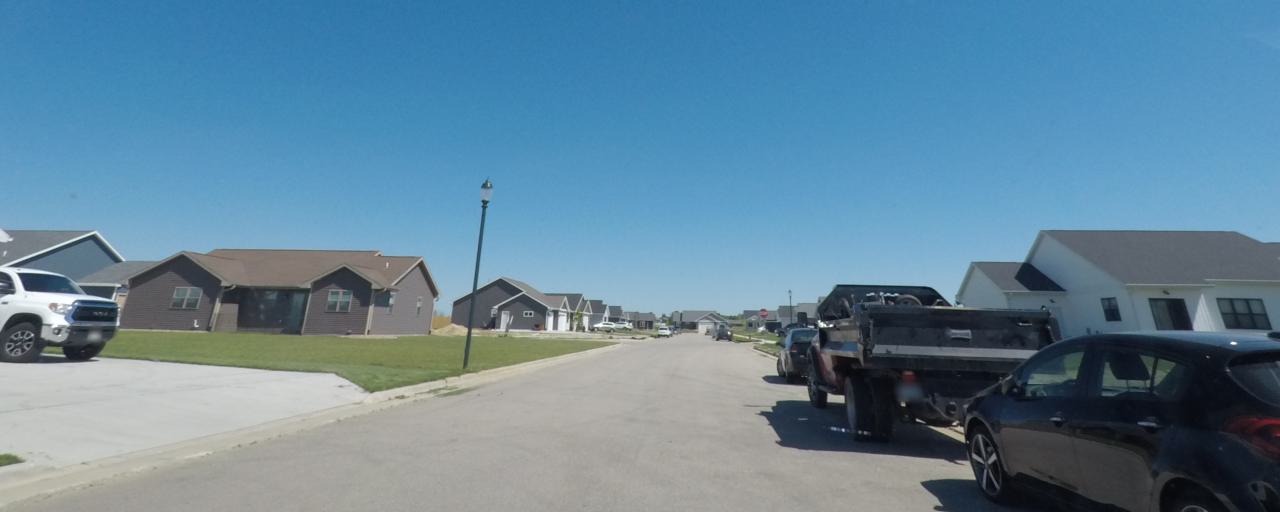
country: US
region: Wisconsin
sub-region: Rock County
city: Evansville
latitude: 42.7737
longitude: -89.3211
